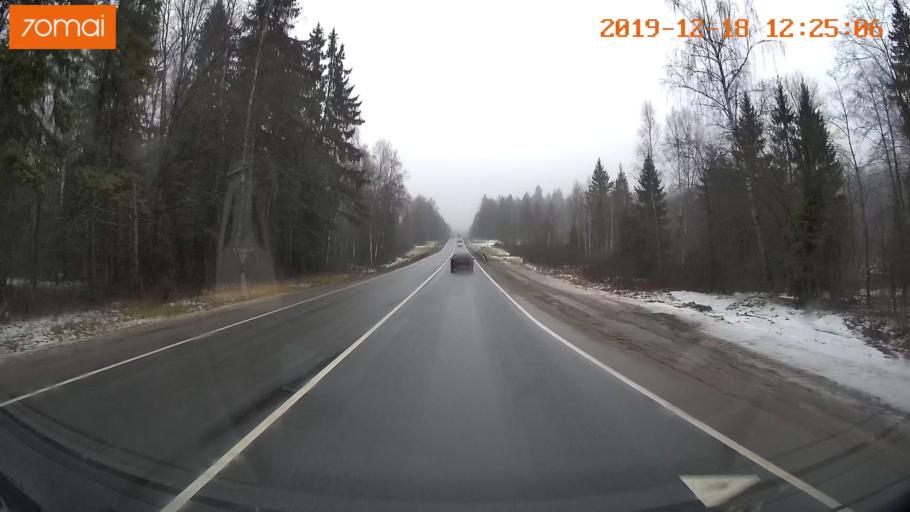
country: RU
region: Moskovskaya
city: Novopetrovskoye
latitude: 56.0334
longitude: 36.5001
